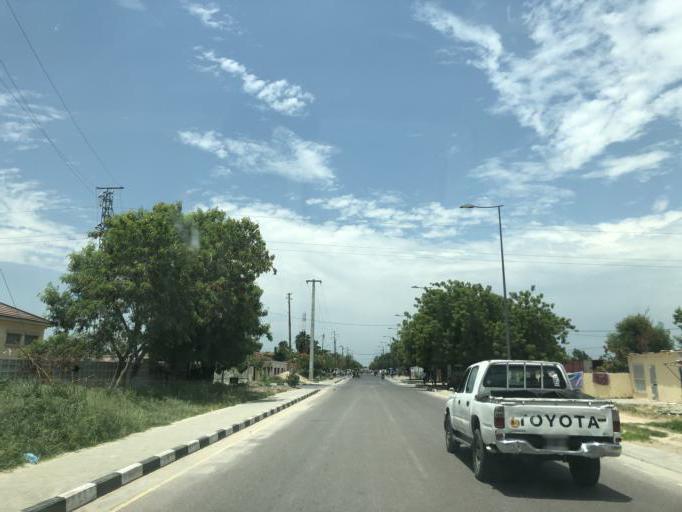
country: AO
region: Cunene
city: Ondjiva
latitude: -17.0695
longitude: 15.7247
